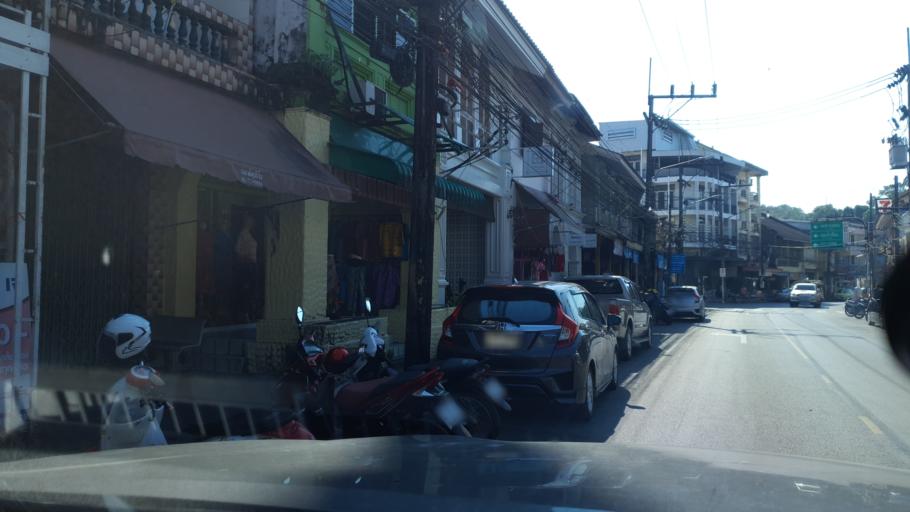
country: TH
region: Ranong
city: Ranong
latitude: 9.9647
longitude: 98.6339
